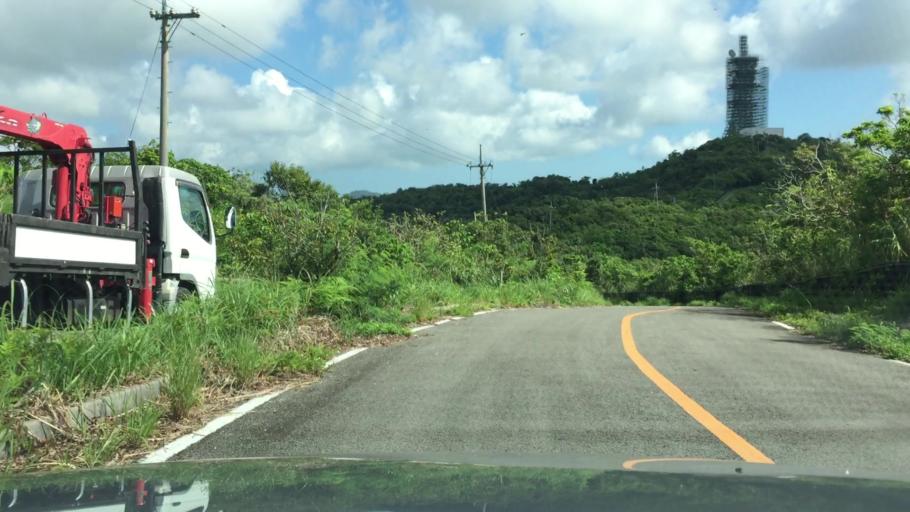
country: JP
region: Okinawa
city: Ishigaki
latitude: 24.3744
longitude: 124.1641
